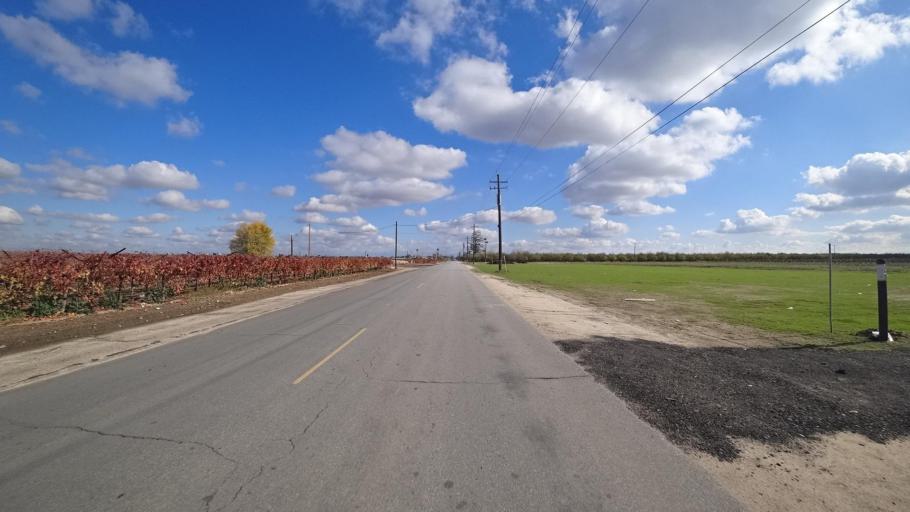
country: US
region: California
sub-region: Kern County
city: McFarland
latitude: 35.6743
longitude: -119.2498
